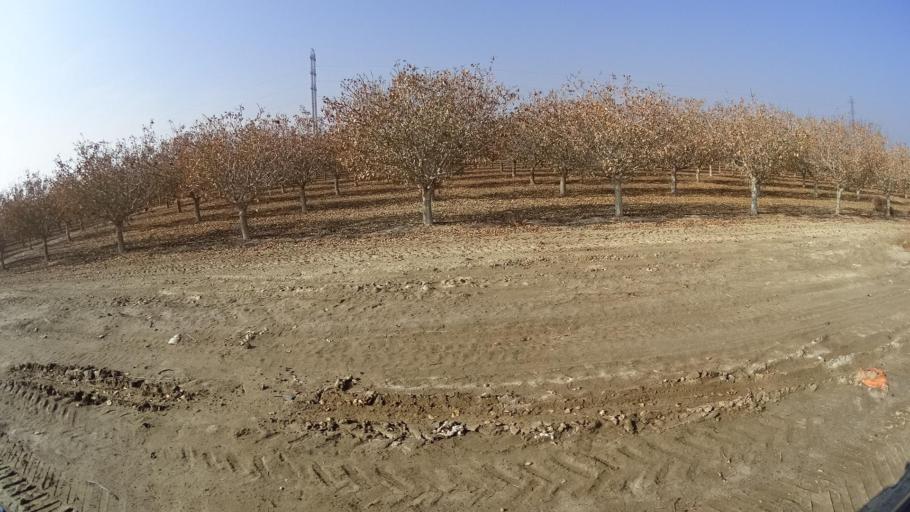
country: US
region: California
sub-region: Kern County
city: Buttonwillow
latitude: 35.4116
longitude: -119.4475
